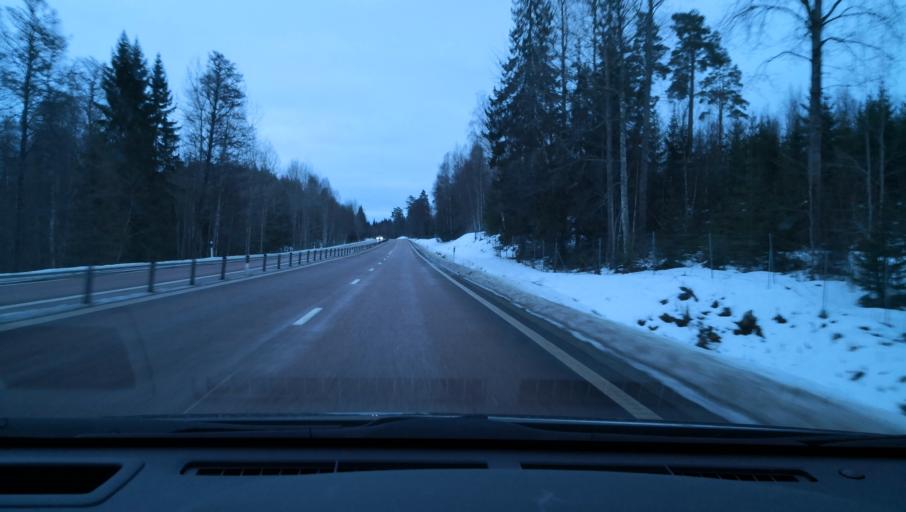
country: SE
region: Vaestmanland
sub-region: Norbergs Kommun
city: Norberg
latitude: 59.9337
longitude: 15.9180
